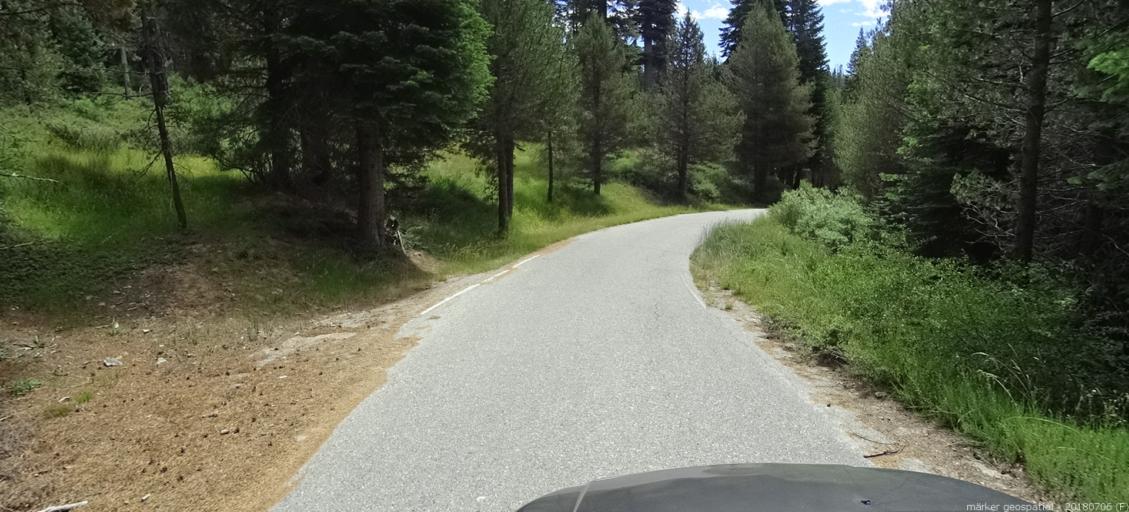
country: US
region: California
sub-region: Madera County
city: Oakhurst
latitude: 37.4334
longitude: -119.4326
